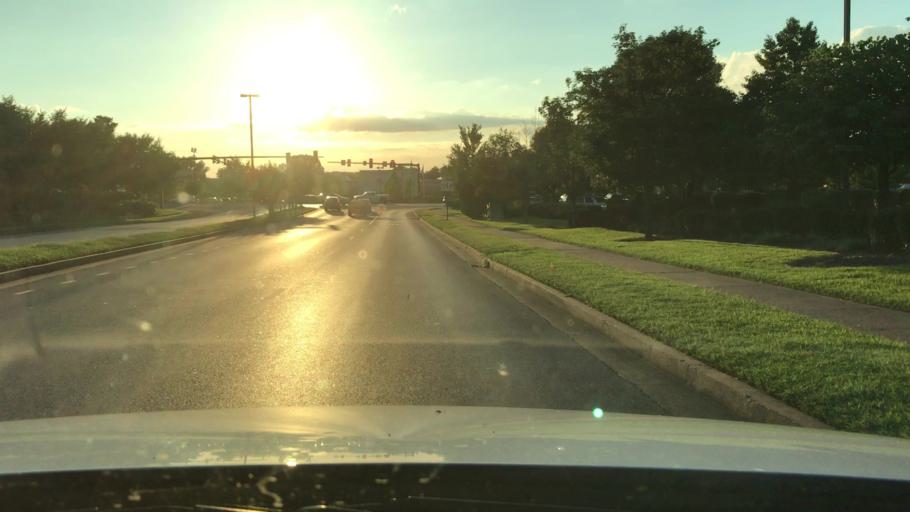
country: US
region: Tennessee
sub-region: Sumner County
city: Hendersonville
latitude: 36.3206
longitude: -86.5981
